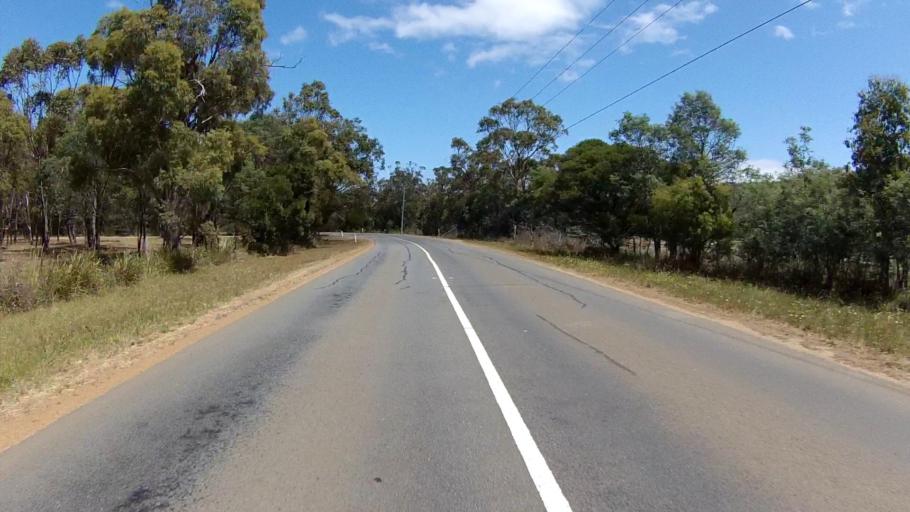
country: AU
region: Tasmania
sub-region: Clarence
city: Sandford
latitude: -42.9452
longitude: 147.4831
